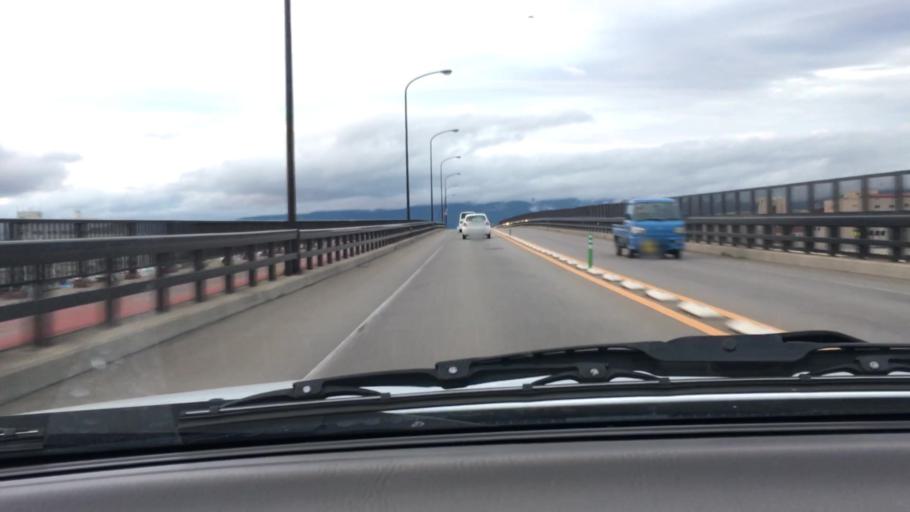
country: JP
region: Hokkaido
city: Hakodate
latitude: 41.7787
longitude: 140.7259
